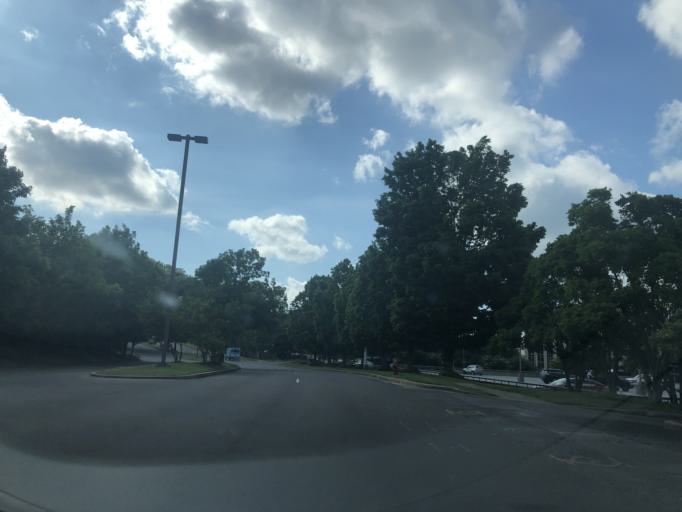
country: US
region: Tennessee
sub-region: Davidson County
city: Forest Hills
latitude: 36.0947
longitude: -86.8230
